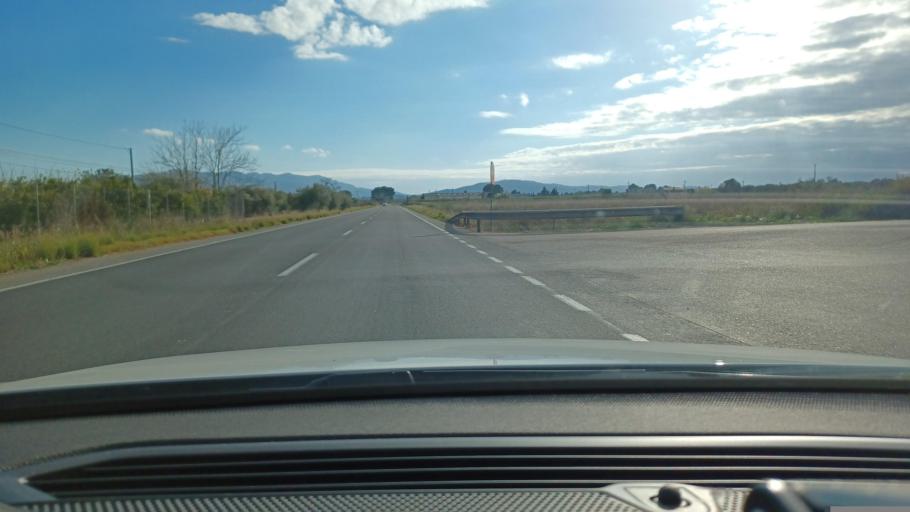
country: ES
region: Catalonia
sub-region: Provincia de Tarragona
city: Santa Barbara
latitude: 40.7324
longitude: 0.5031
